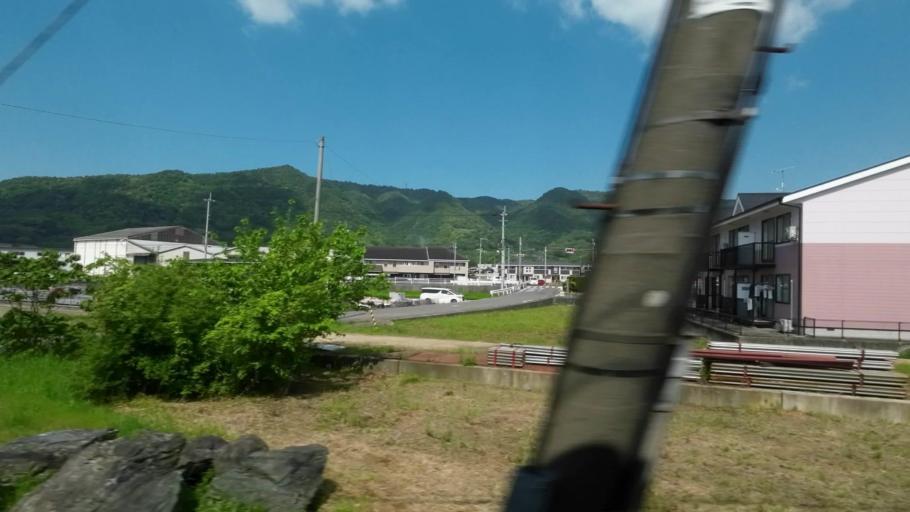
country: JP
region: Kagawa
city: Kan'onjicho
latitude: 34.1624
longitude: 133.6894
